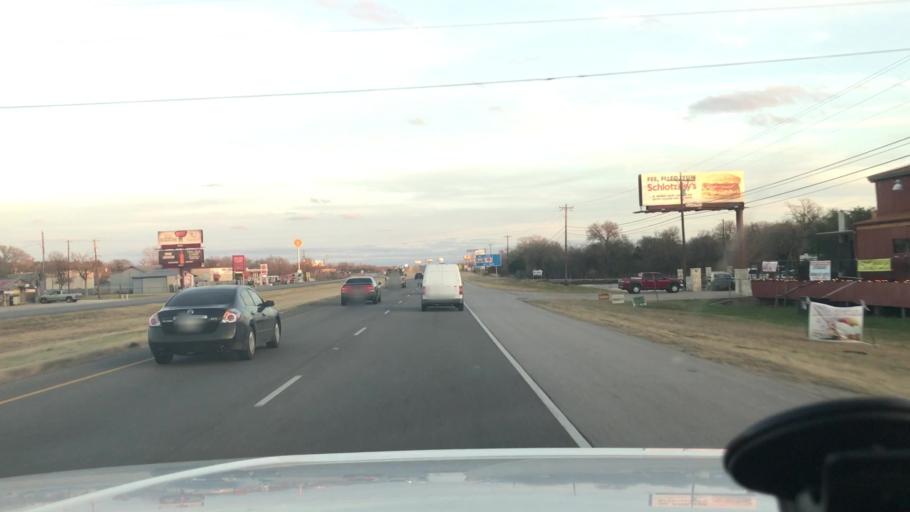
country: US
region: Texas
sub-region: Bastrop County
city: Wyldwood
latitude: 30.1175
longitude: -97.4246
